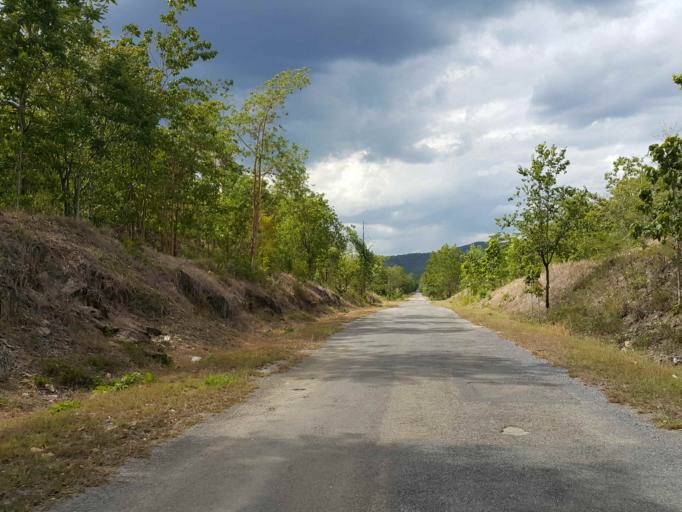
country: TH
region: Sukhothai
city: Thung Saliam
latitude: 17.3315
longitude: 99.4239
